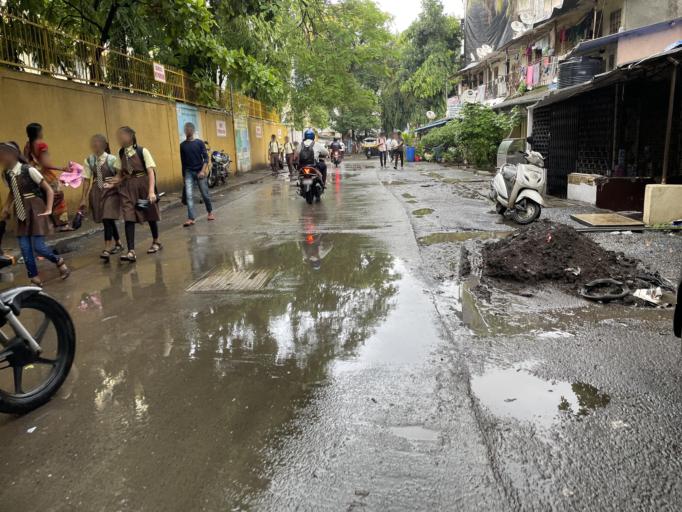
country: IN
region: Maharashtra
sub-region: Mumbai Suburban
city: Borivli
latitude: 19.2542
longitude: 72.8599
